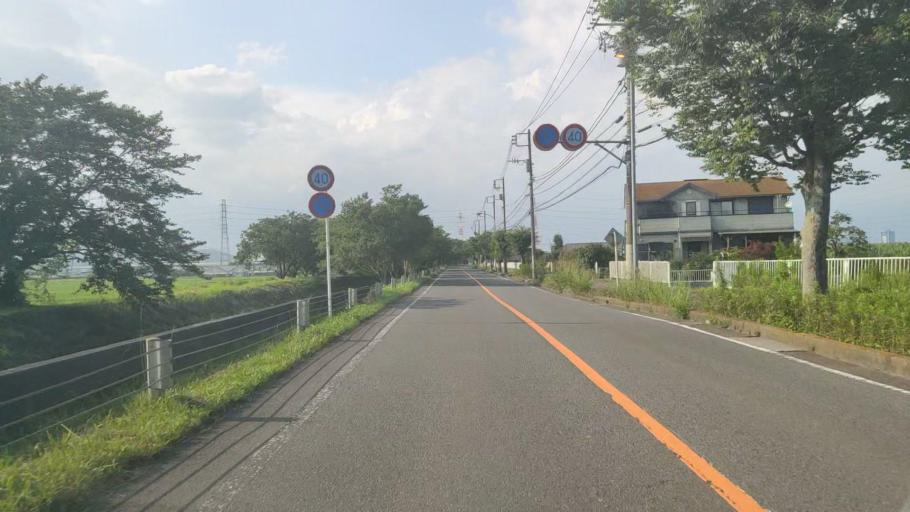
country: JP
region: Kanagawa
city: Isehara
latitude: 35.3925
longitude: 139.3379
